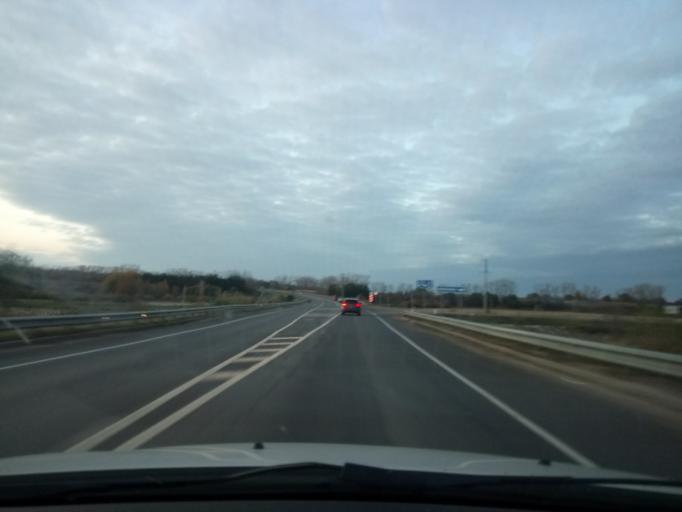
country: RU
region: Nizjnij Novgorod
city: Bol'shoye Murashkino
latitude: 55.8815
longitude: 44.7480
